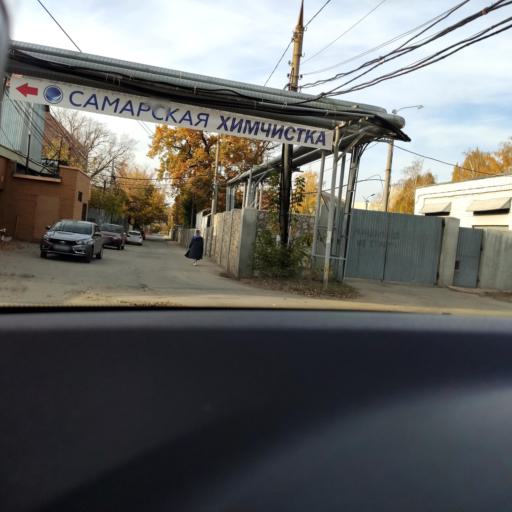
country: RU
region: Samara
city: Samara
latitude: 53.2739
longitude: 50.1935
